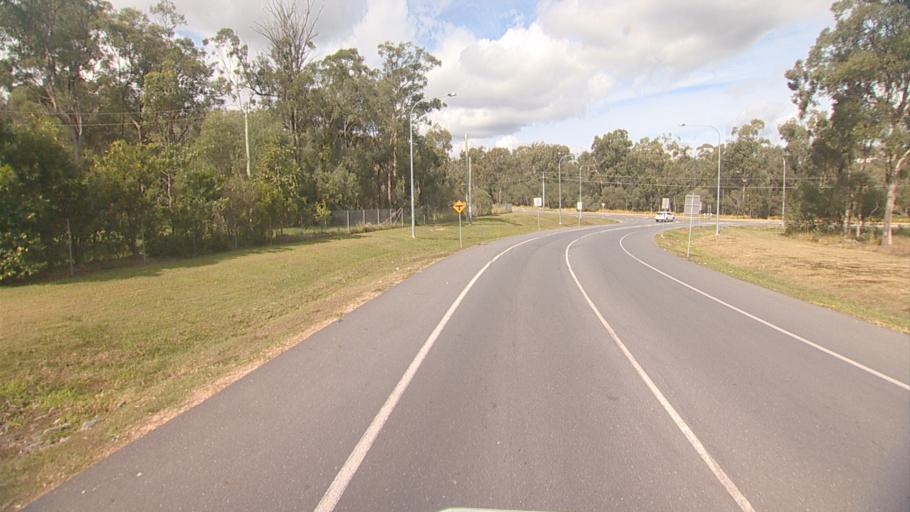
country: AU
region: Queensland
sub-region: Logan
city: Logan Reserve
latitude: -27.6920
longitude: 153.0703
